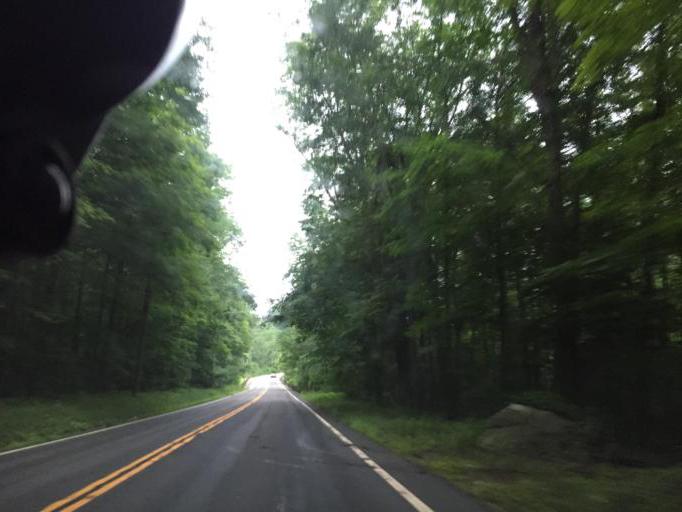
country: US
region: Connecticut
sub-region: Litchfield County
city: Canaan
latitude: 41.9367
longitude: -73.2967
